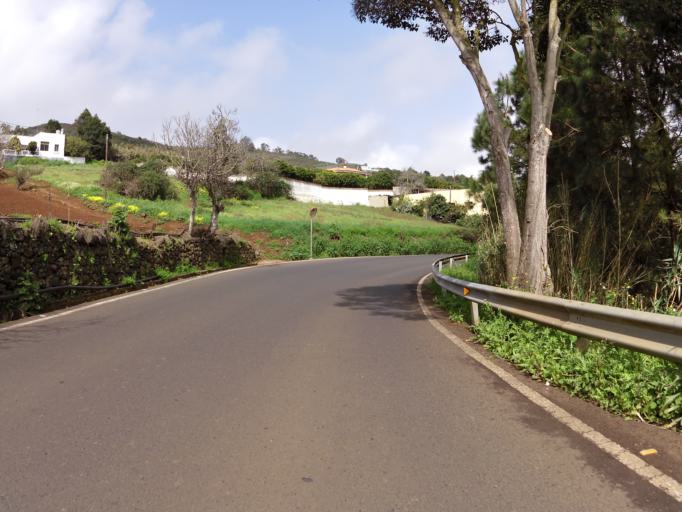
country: ES
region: Canary Islands
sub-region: Provincia de Las Palmas
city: Teror
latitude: 28.0803
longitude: -15.5423
